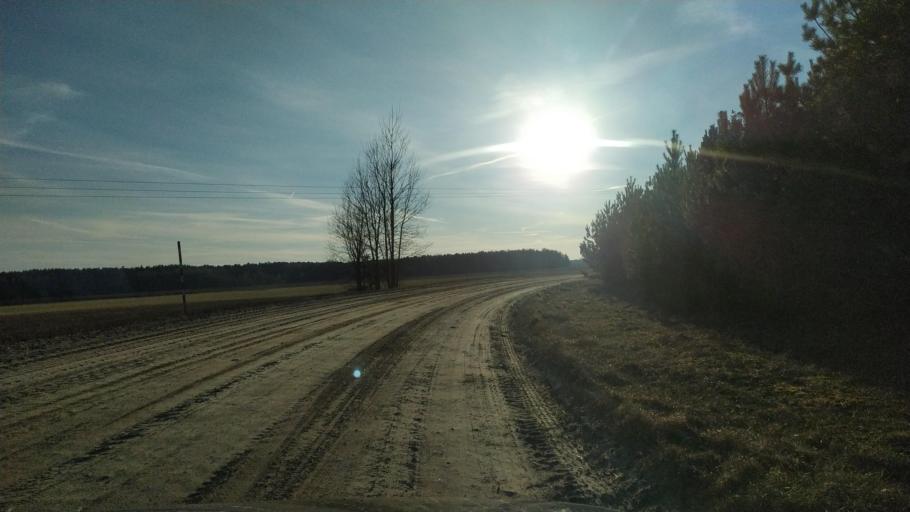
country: BY
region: Brest
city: Pruzhany
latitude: 52.5459
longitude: 24.2844
